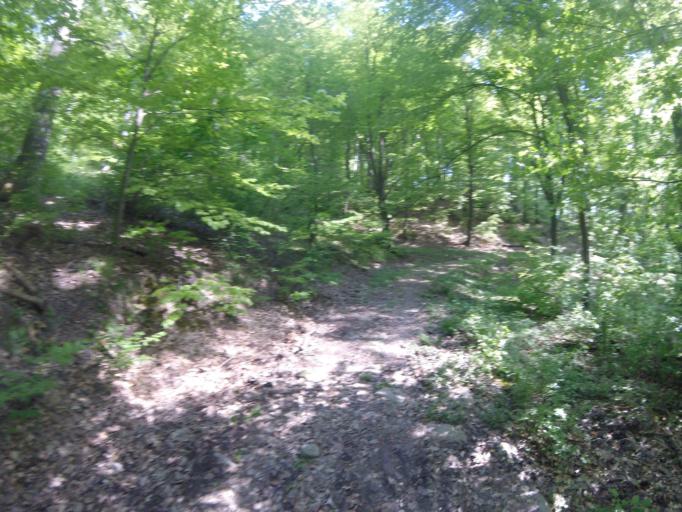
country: HU
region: Pest
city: Pilisszentkereszt
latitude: 47.7059
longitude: 18.8996
